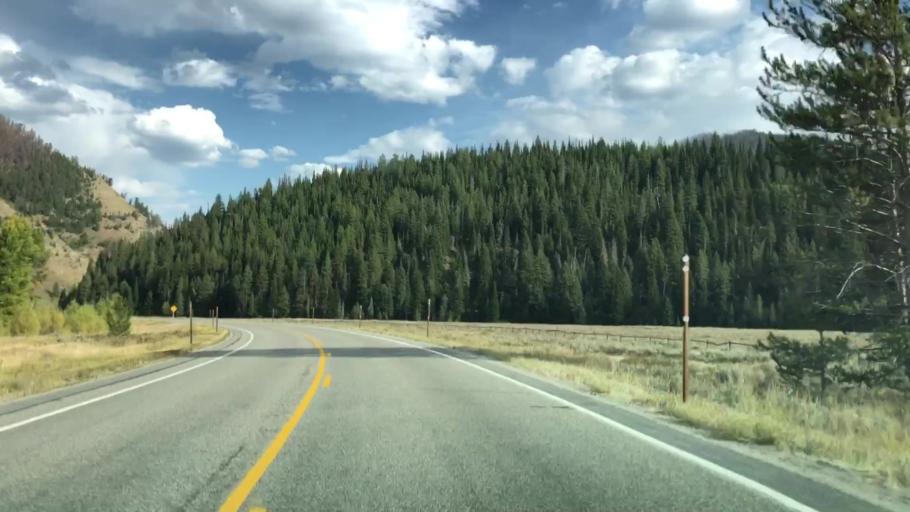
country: US
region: Wyoming
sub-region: Teton County
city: Hoback
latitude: 43.2530
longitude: -110.5046
